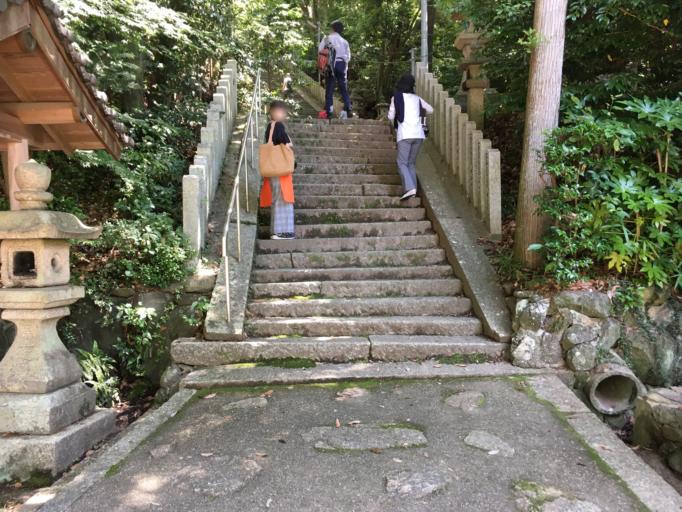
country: JP
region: Nara
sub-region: Ikoma-shi
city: Ikoma
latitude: 34.7445
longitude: 135.7221
